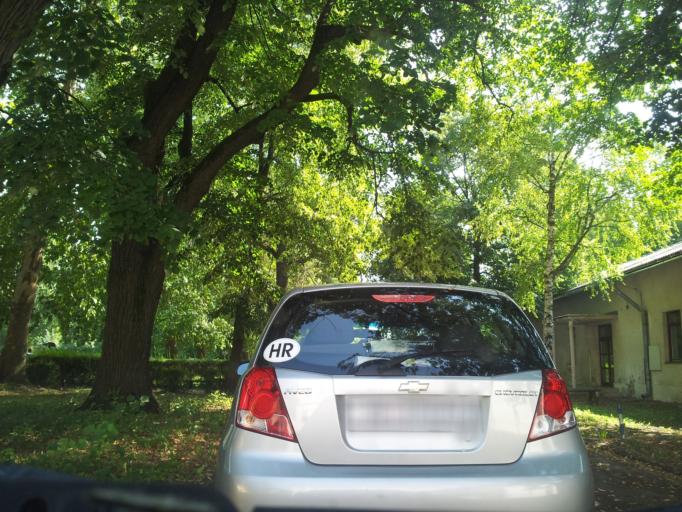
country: HR
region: Osjecko-Baranjska
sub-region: Grad Osijek
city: Osijek
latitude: 45.5563
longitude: 18.7121
